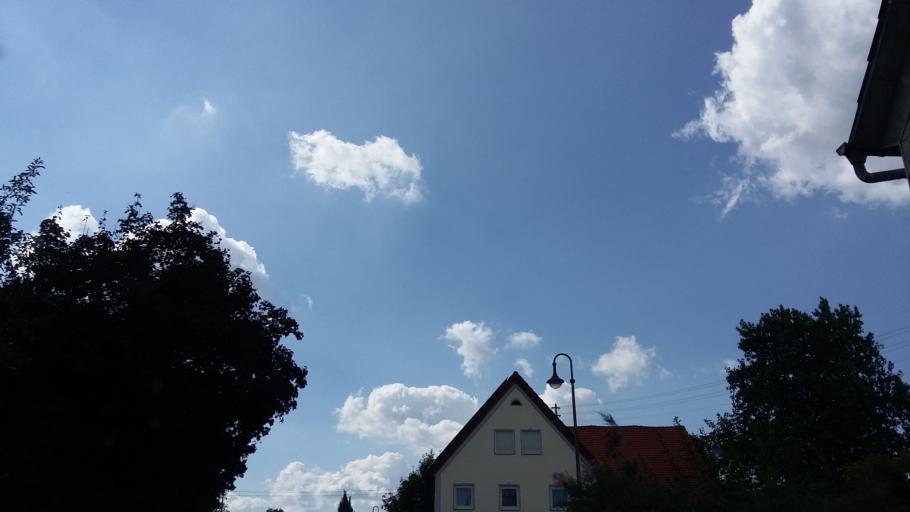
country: DE
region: Bavaria
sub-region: Swabia
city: Pfaffenhofen an der Roth
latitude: 48.3576
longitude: 10.1850
